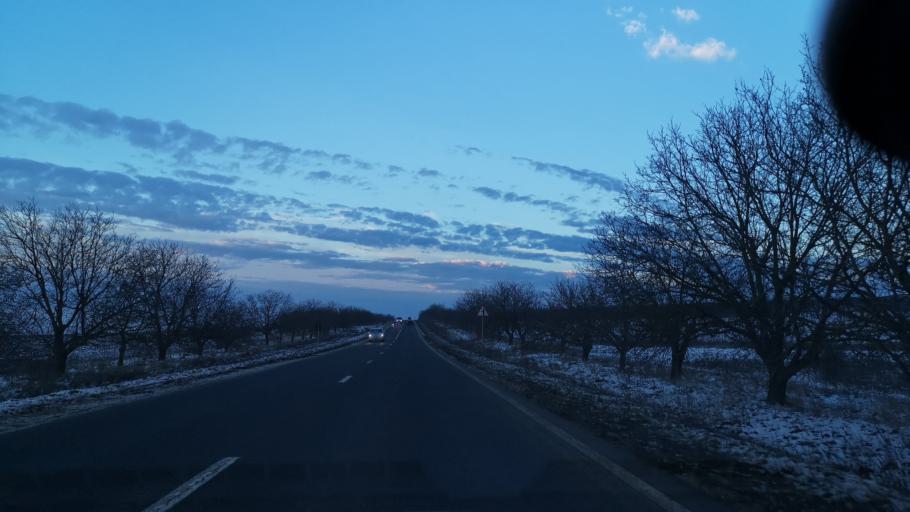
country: MD
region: Rezina
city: Saharna
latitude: 47.6110
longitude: 28.8308
